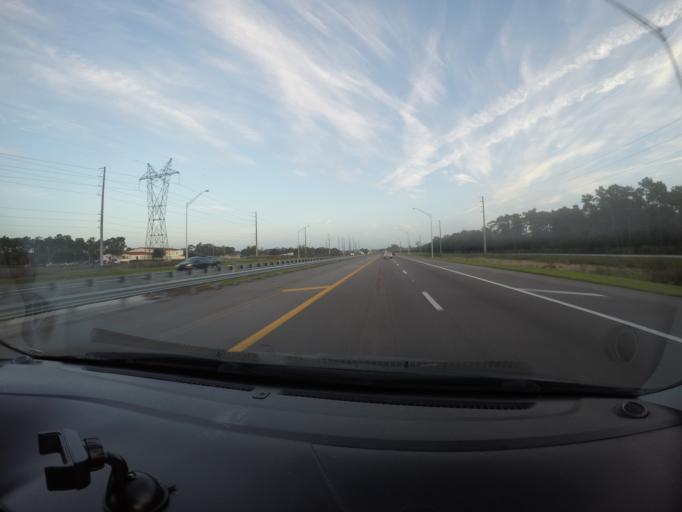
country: US
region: Florida
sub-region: Orange County
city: Azalea Park
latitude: 28.5304
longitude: -81.2508
